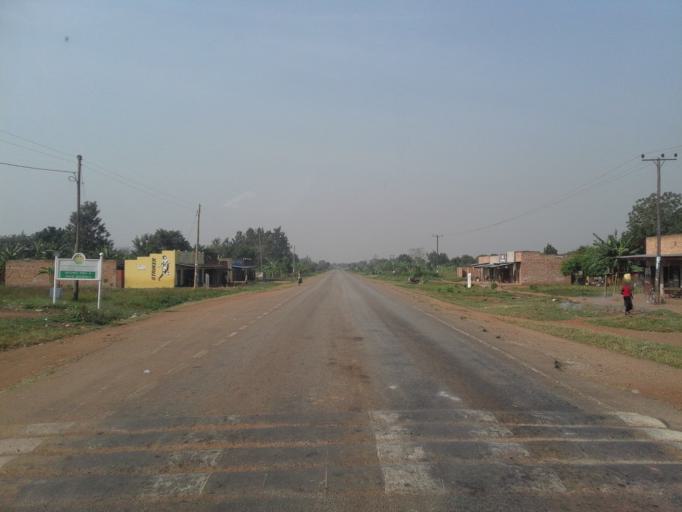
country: UG
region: Eastern Region
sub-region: Mbale District
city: Mbale
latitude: 1.0628
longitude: 34.0781
